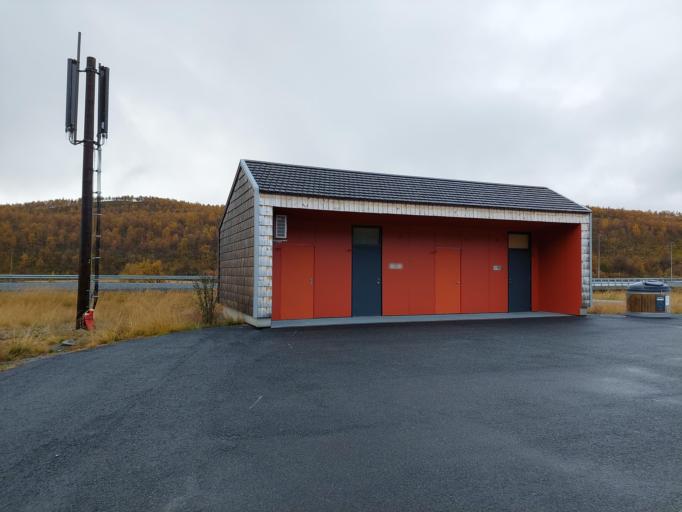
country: NO
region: Sogn og Fjordane
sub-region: Ardal
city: Farnes
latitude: 61.1805
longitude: 8.0938
